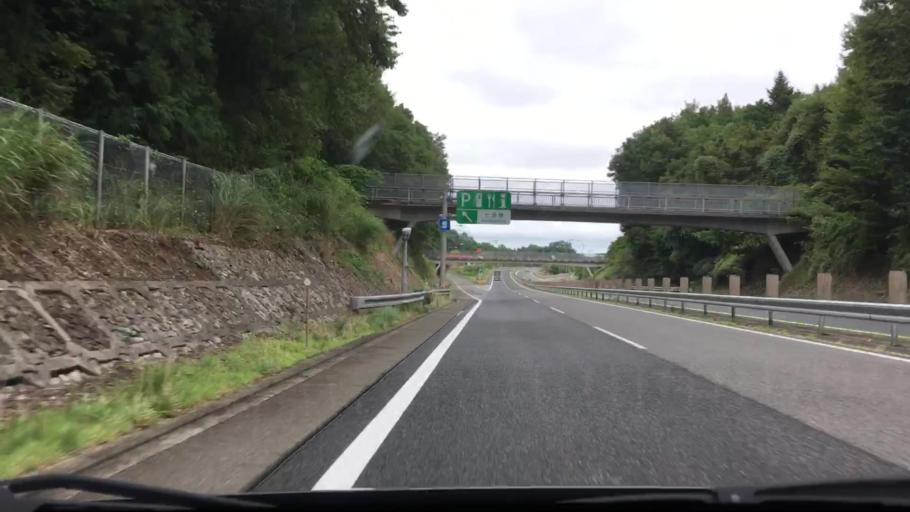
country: JP
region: Hiroshima
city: Shobara
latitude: 34.8299
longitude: 132.9629
